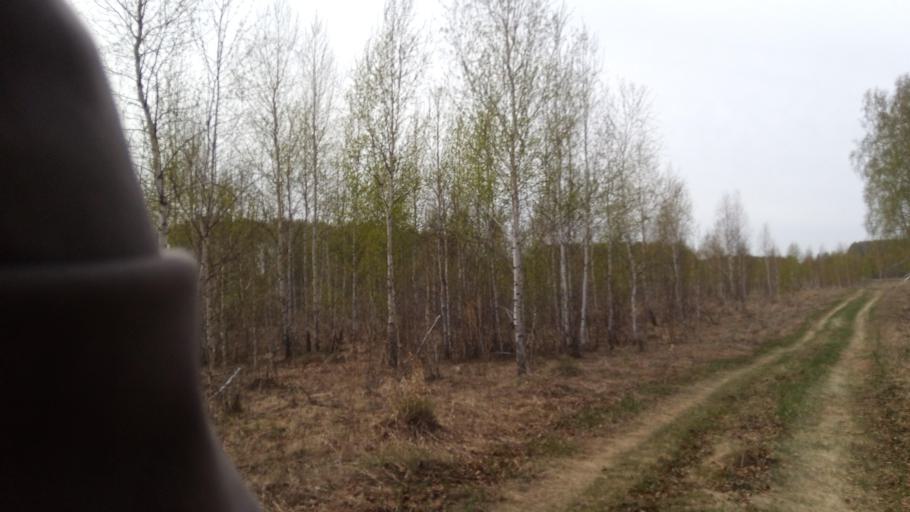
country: RU
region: Chelyabinsk
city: Timiryazevskiy
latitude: 55.0066
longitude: 60.8571
